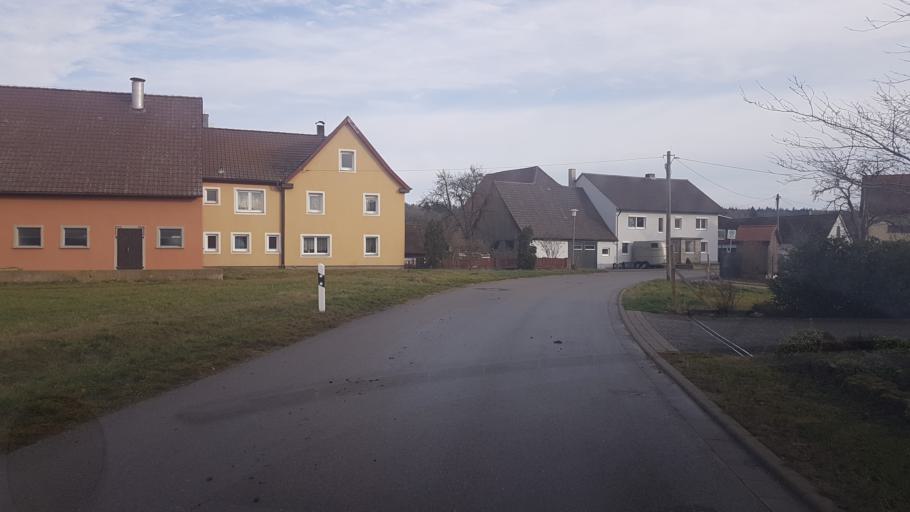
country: DE
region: Bavaria
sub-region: Regierungsbezirk Mittelfranken
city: Wettringen
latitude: 49.2340
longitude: 10.1502
